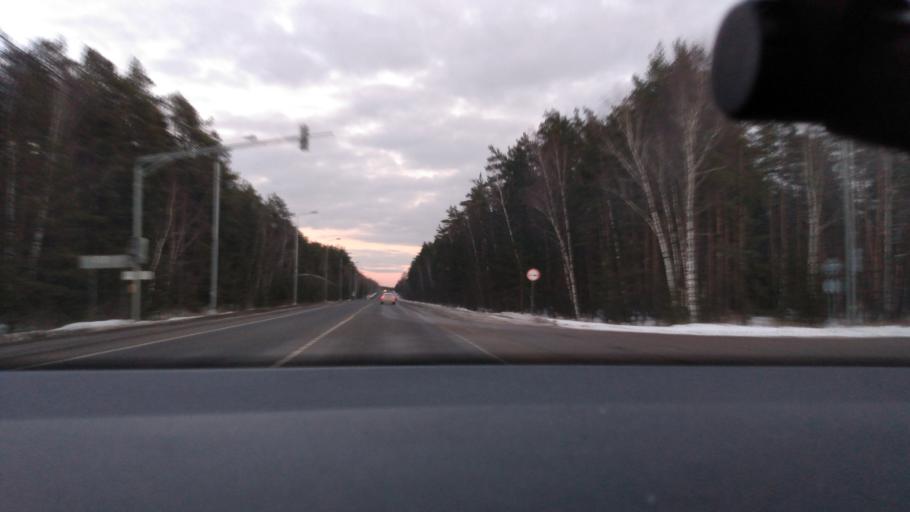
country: RU
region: Moskovskaya
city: Il'inskiy Pogost
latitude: 55.4881
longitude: 38.8933
